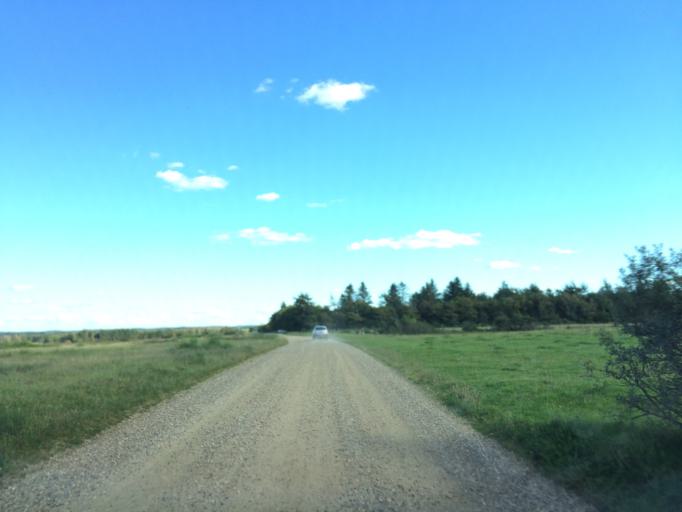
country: DK
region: Central Jutland
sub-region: Holstebro Kommune
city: Holstebro
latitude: 56.2762
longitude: 8.4926
